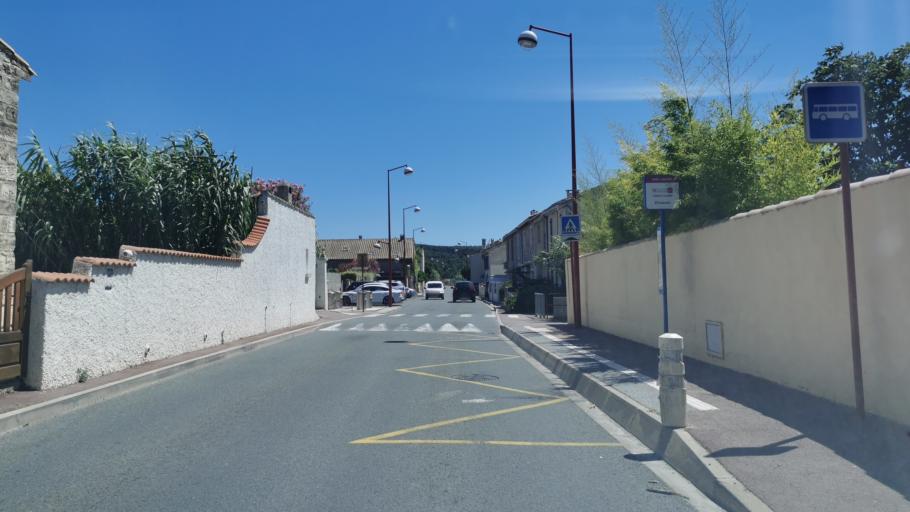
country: FR
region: Languedoc-Roussillon
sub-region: Departement de l'Aude
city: Vinassan
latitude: 43.2004
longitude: 3.0745
